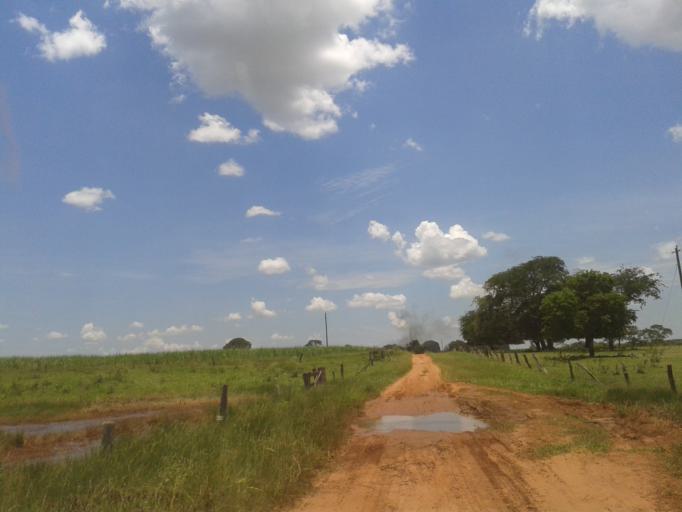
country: BR
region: Minas Gerais
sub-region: Santa Vitoria
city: Santa Vitoria
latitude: -19.2260
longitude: -50.4614
